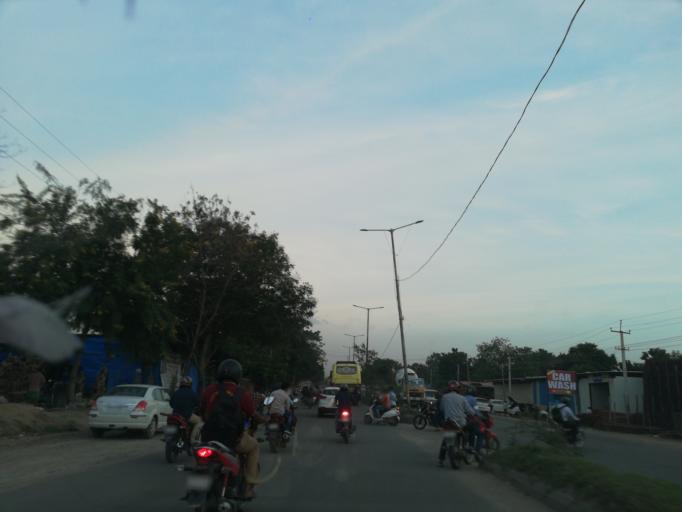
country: IN
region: Telangana
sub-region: Medak
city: Serilingampalle
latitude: 17.5184
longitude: 78.3564
